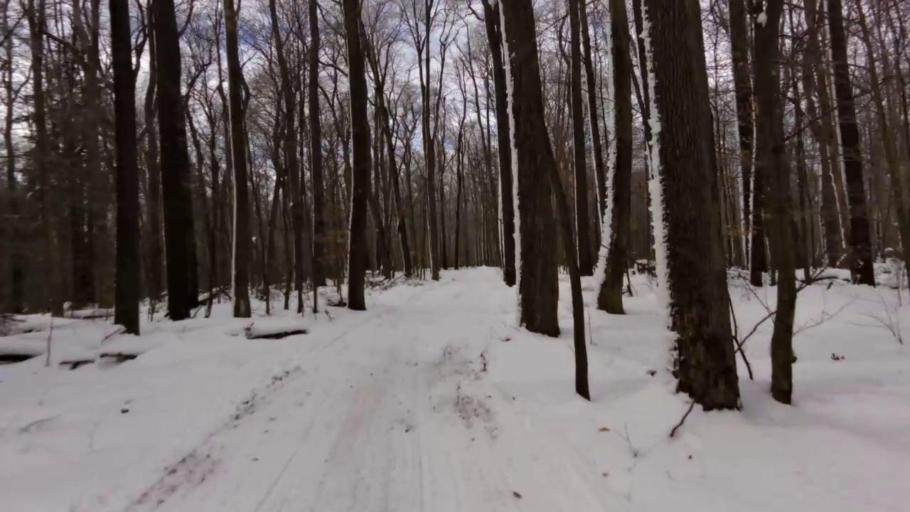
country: US
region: New York
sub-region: Cattaraugus County
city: Salamanca
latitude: 42.0353
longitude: -78.7521
